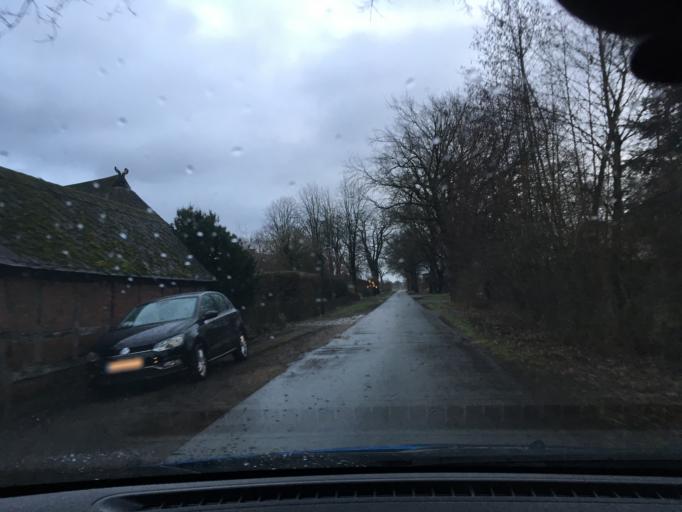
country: DE
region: Lower Saxony
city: Ludersburg
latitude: 53.3089
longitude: 10.6089
